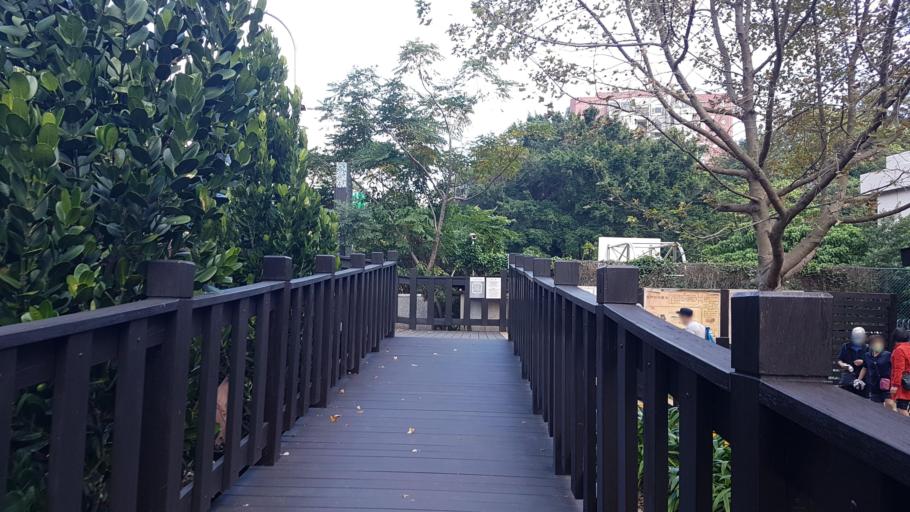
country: TW
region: Taipei
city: Taipei
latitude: 25.1417
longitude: 121.5095
